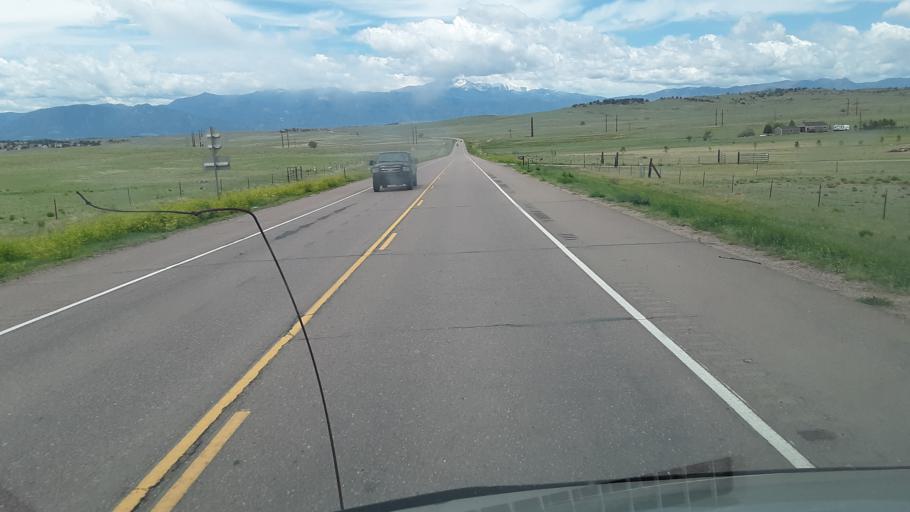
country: US
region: Colorado
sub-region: El Paso County
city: Cimarron Hills
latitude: 38.8388
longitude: -104.6116
